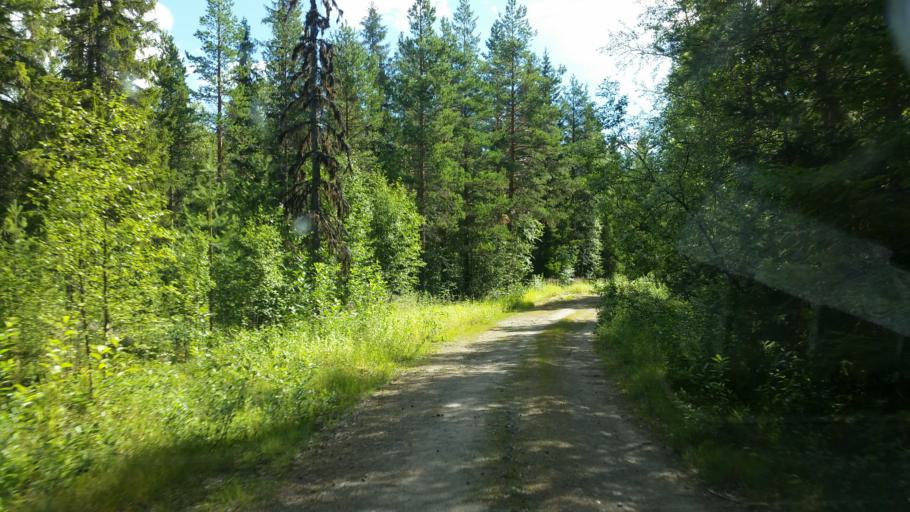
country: SE
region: Vaesternorrland
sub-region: Ange Kommun
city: Ange
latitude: 62.2325
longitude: 15.7353
